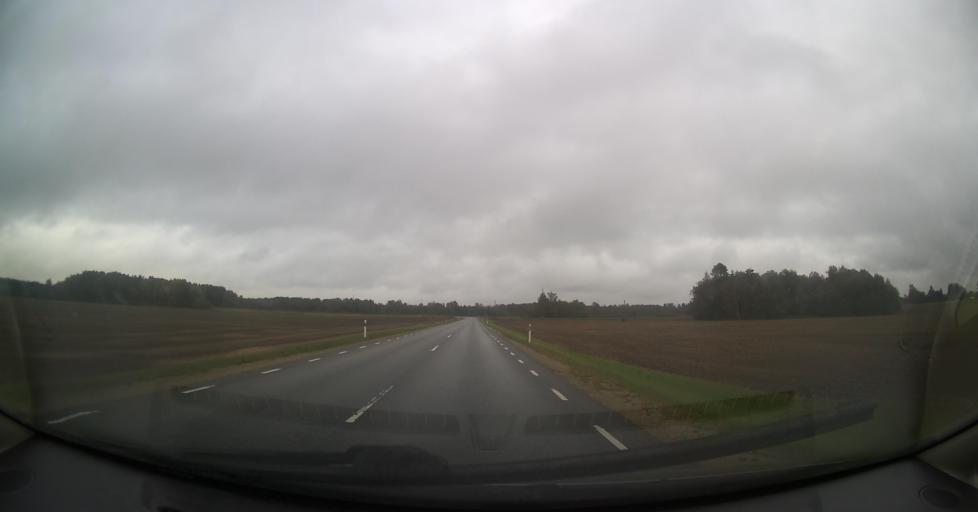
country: EE
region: Harju
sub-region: Anija vald
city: Kehra
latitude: 59.2595
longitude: 25.3396
